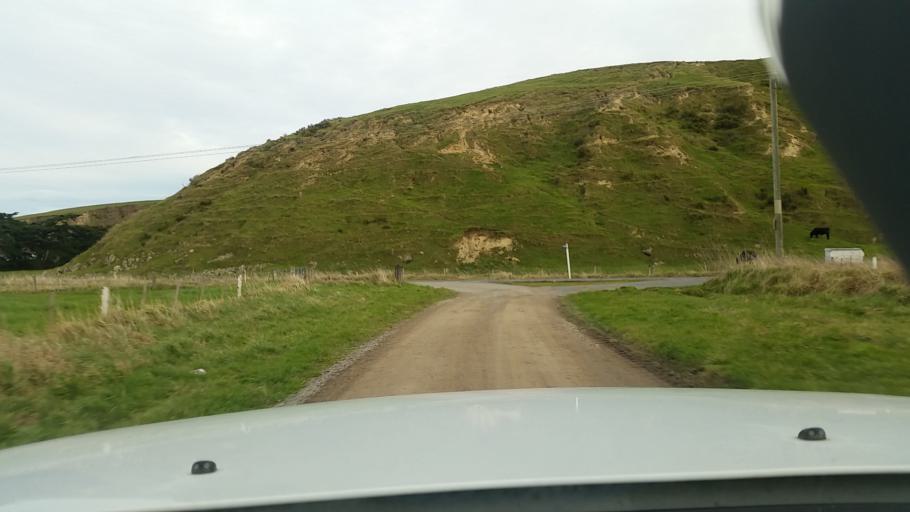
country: NZ
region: Canterbury
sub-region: Selwyn District
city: Lincoln
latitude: -43.7182
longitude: 172.5991
